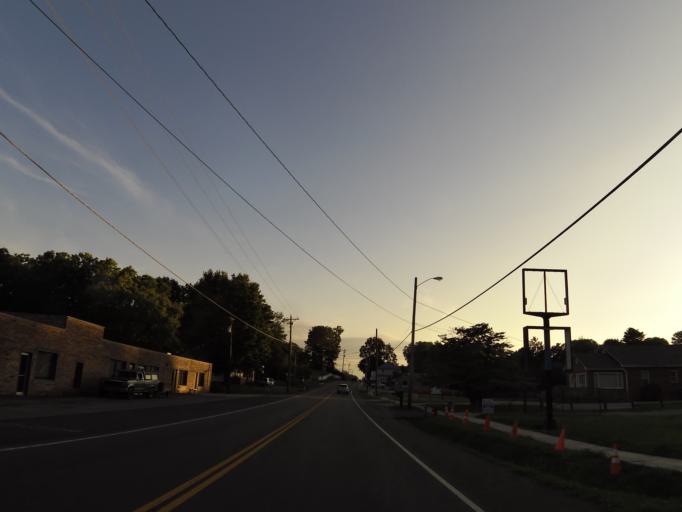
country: US
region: Tennessee
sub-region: Jefferson County
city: Dandridge
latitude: 36.0212
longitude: -83.4079
